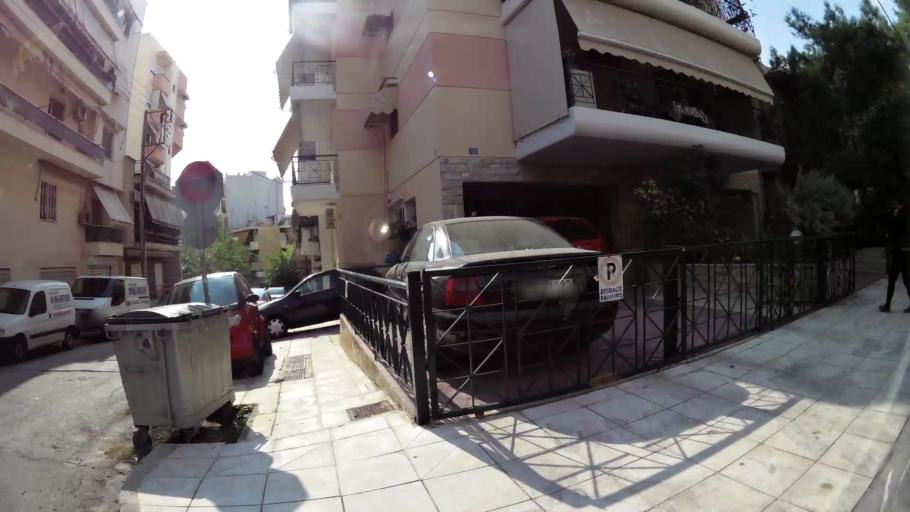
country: GR
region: Attica
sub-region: Nomarchia Athinas
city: Nea Smyrni
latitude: 37.9375
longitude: 23.7151
